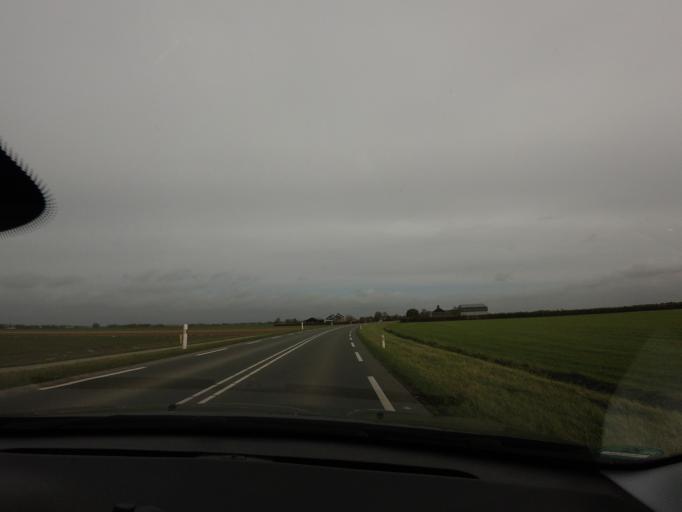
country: NL
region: Overijssel
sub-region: Gemeente Steenwijkerland
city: Vollenhove
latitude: 52.7136
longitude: 5.8802
